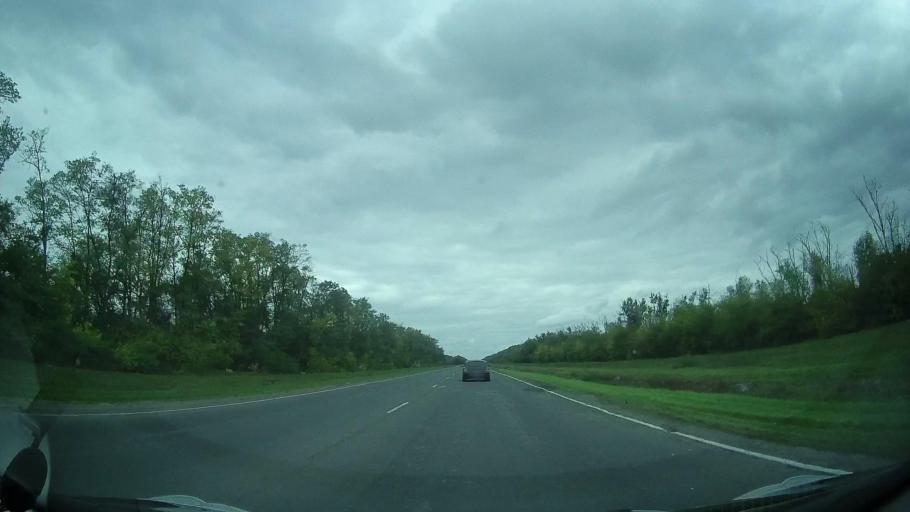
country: RU
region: Rostov
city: Yegorlykskaya
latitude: 46.5965
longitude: 40.6226
